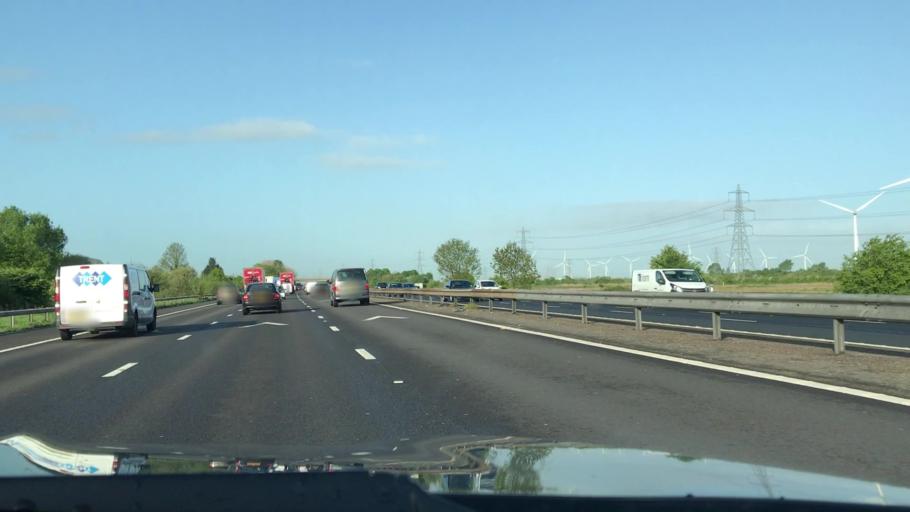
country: GB
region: England
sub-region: Cheshire West and Chester
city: Frodsham
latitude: 53.2993
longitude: -2.7274
